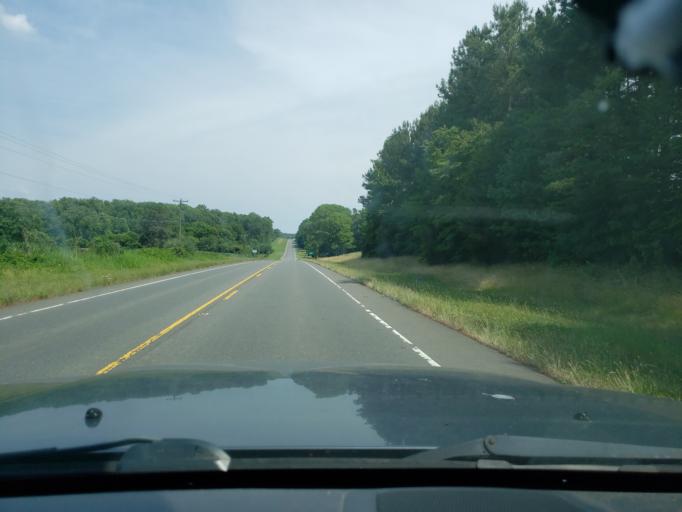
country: US
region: North Carolina
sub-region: Alamance County
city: Saxapahaw
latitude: 35.9601
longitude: -79.2646
